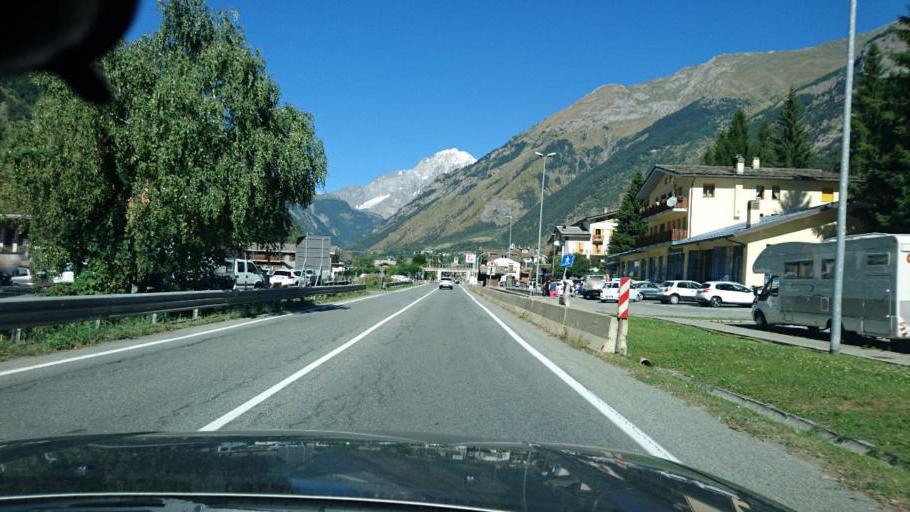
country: IT
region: Aosta Valley
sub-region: Valle d'Aosta
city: Morgex
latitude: 45.7540
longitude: 7.0434
